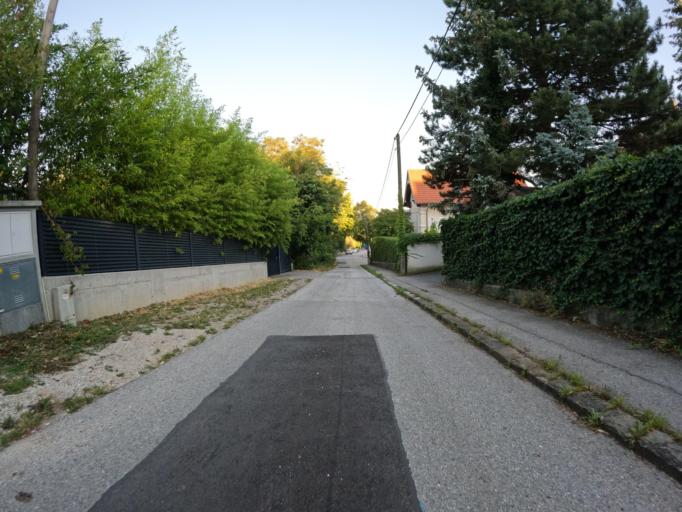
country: AT
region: Lower Austria
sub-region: Politischer Bezirk Baden
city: Baden
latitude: 48.0148
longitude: 16.2393
